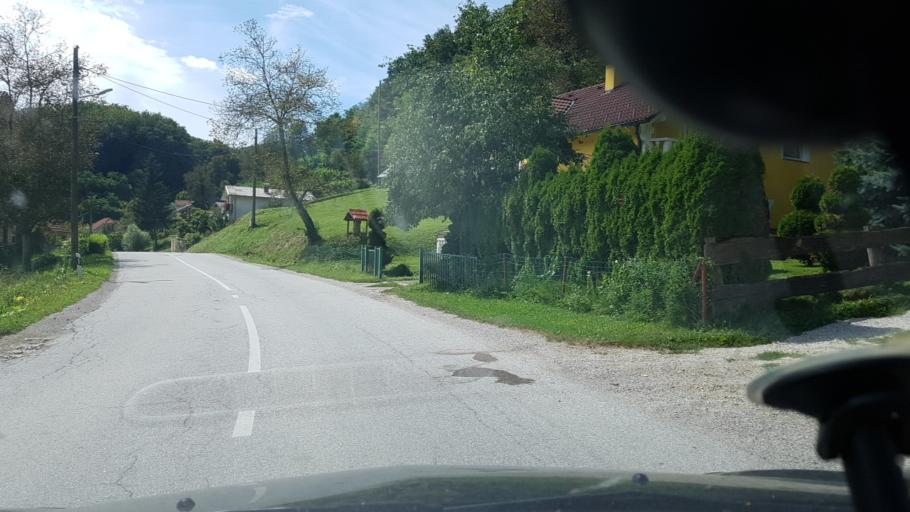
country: HR
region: Krapinsko-Zagorska
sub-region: Grad Krapina
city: Krapina
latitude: 46.1971
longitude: 15.8681
